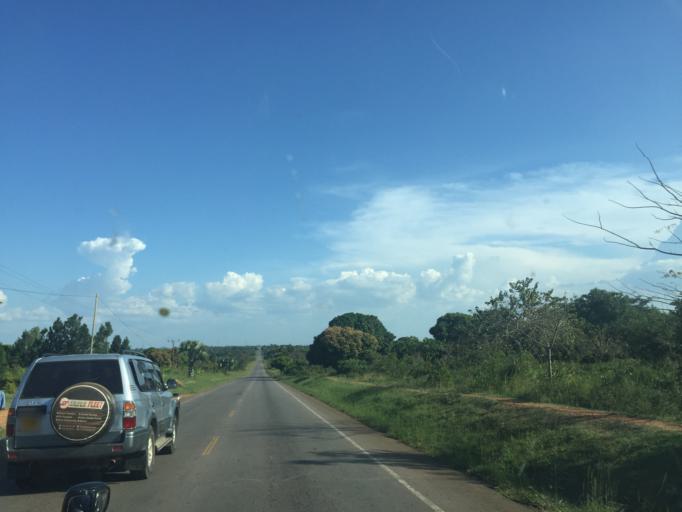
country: UG
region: Central Region
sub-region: Nakasongola District
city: Nakasongola
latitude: 1.2761
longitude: 32.4392
